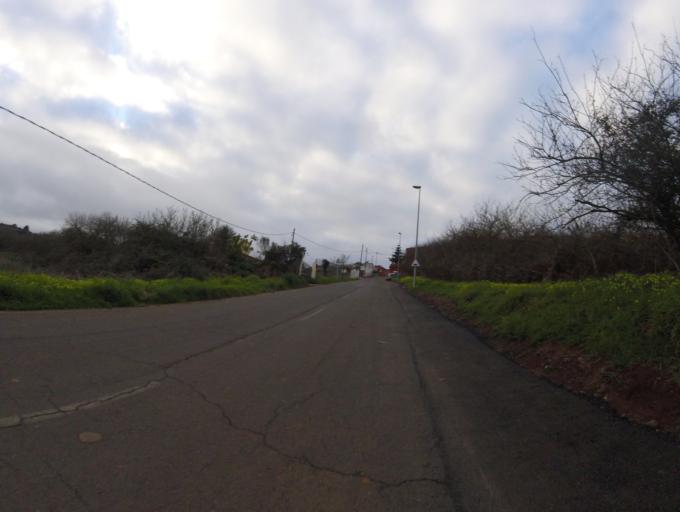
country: ES
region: Canary Islands
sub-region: Provincia de Santa Cruz de Tenerife
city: La Laguna
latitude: 28.4535
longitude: -16.3589
